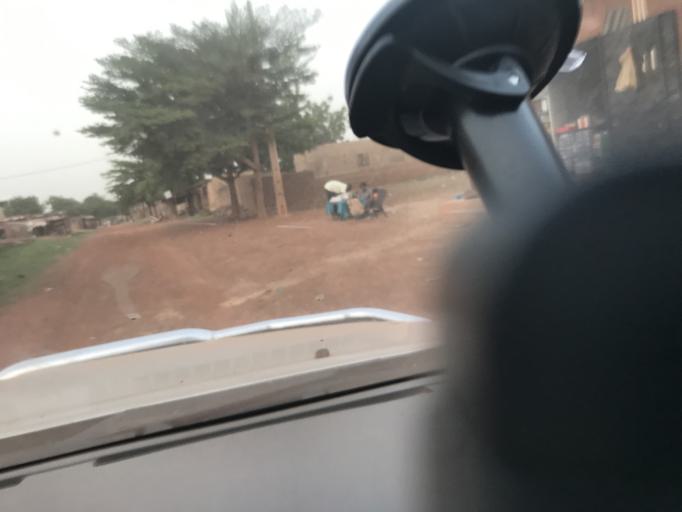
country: ML
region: Bamako
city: Bamako
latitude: 12.6529
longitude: -7.8900
